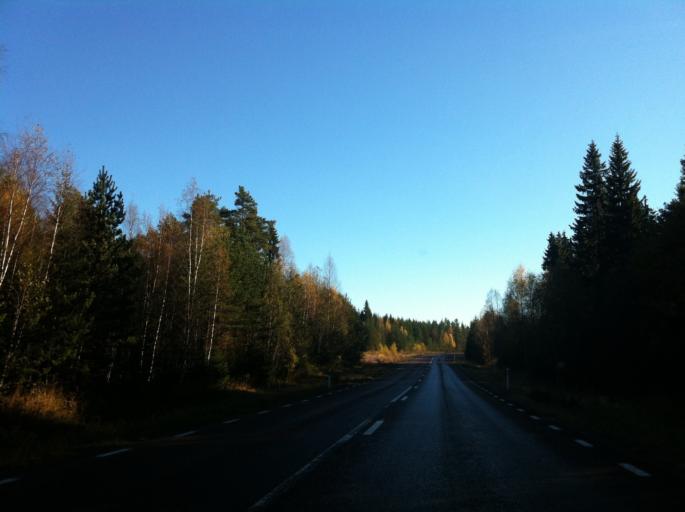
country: SE
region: Dalarna
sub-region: Alvdalens Kommun
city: AElvdalen
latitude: 61.1709
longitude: 14.1053
